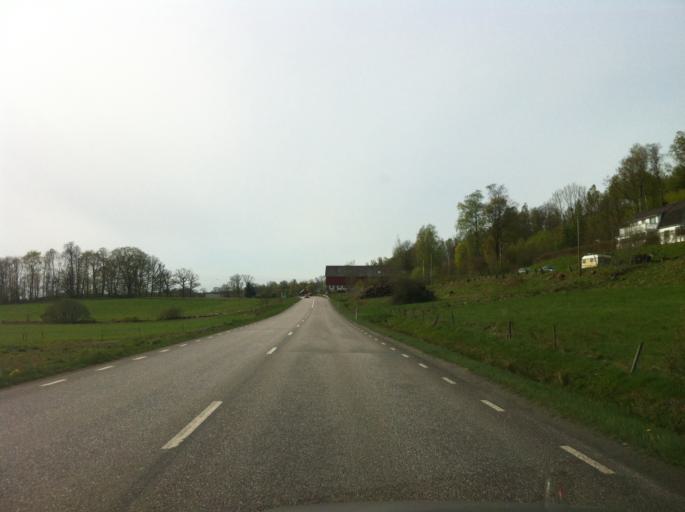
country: SE
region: Vaestra Goetaland
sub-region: Harryda Kommun
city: Ravlanda
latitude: 57.5409
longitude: 12.5324
